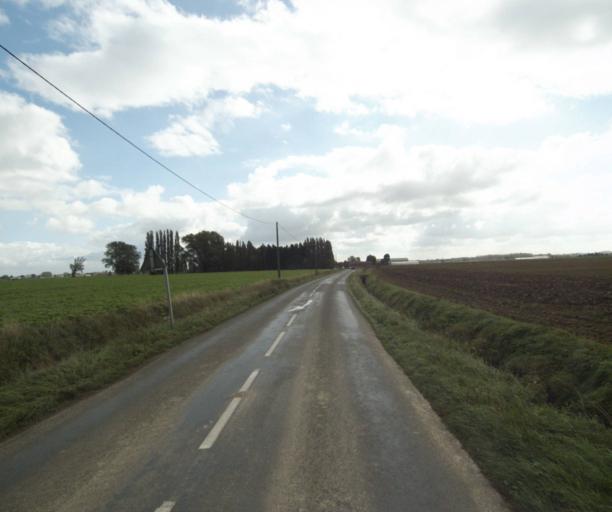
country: FR
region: Nord-Pas-de-Calais
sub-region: Departement du Nord
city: Houplines
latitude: 50.6950
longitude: 2.9367
